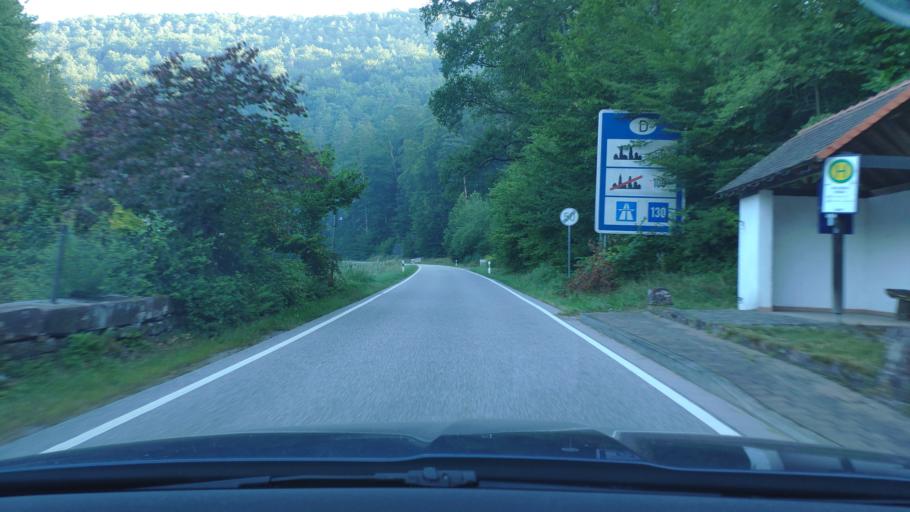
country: DE
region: Rheinland-Pfalz
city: Hirschthal
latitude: 49.0526
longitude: 7.7599
